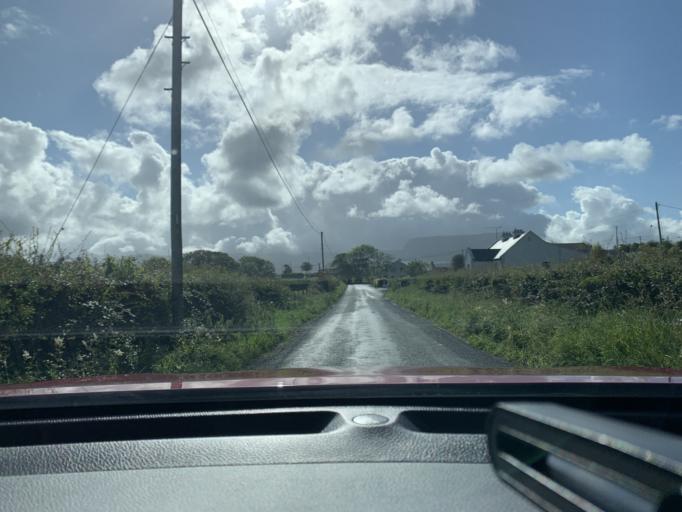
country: IE
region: Connaught
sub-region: Sligo
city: Strandhill
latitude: 54.3917
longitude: -8.5457
